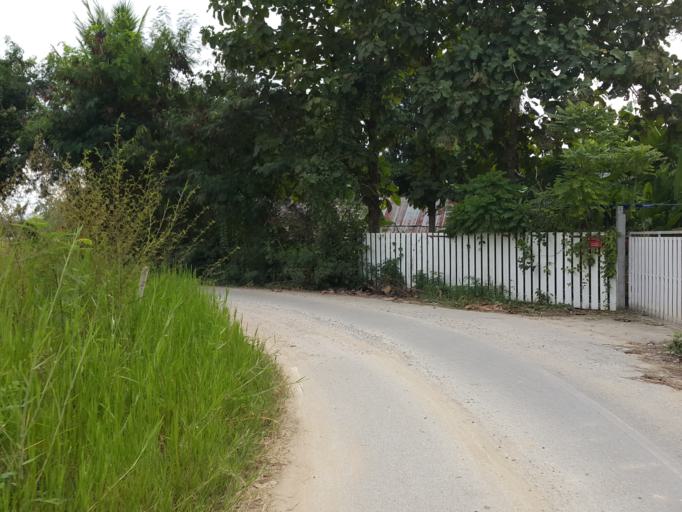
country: TH
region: Chiang Mai
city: San Kamphaeng
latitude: 18.7736
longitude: 99.1029
